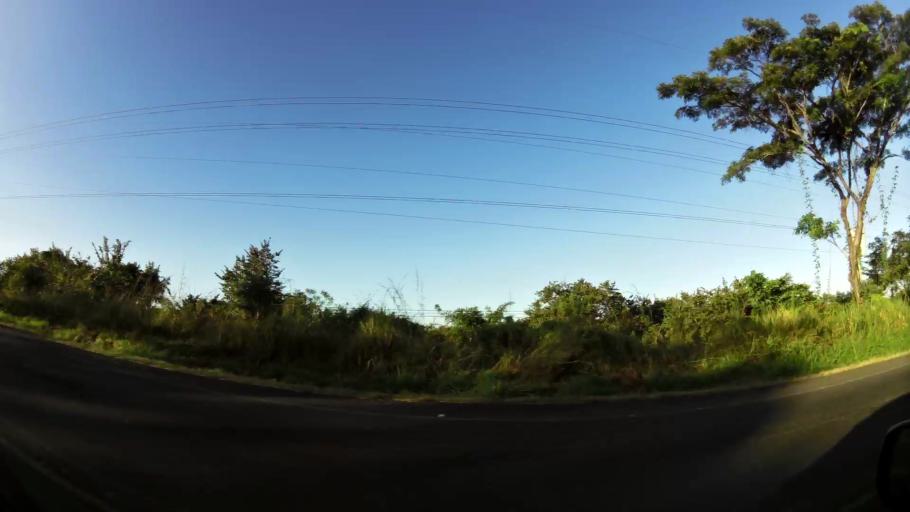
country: CR
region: Puntarenas
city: Esparza
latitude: 9.9990
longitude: -84.7197
